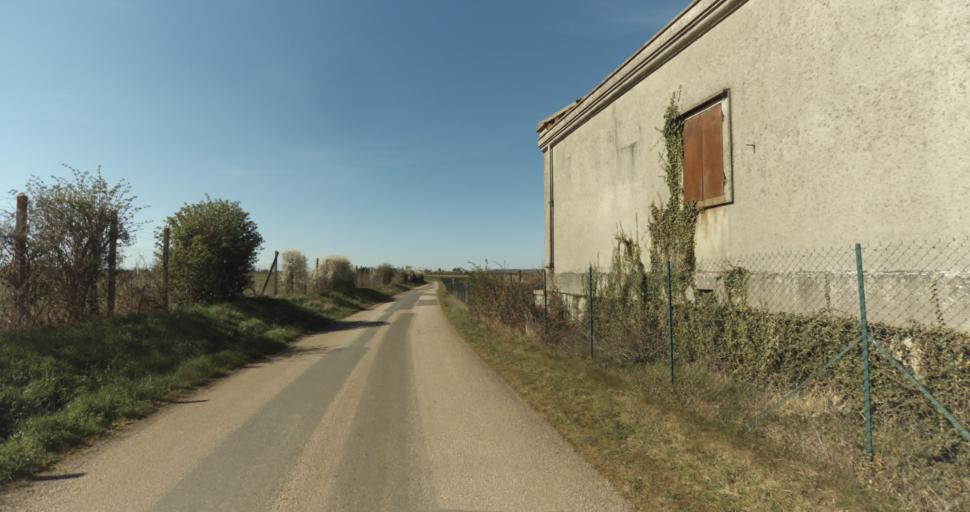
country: FR
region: Lower Normandy
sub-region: Departement du Calvados
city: Saint-Pierre-sur-Dives
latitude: 49.0485
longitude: -0.0508
